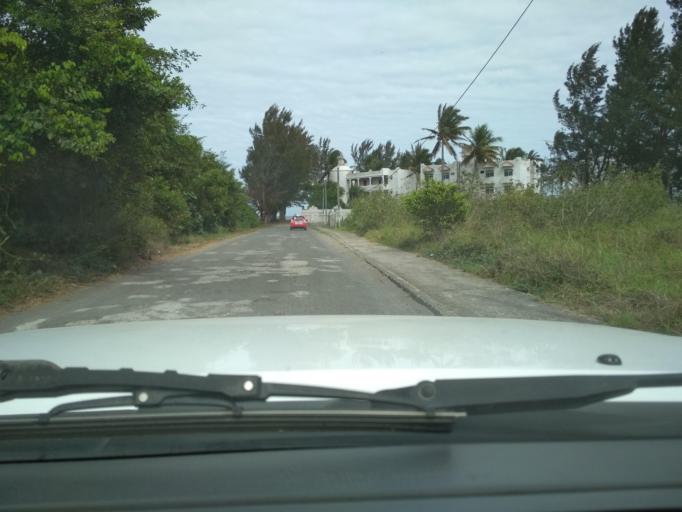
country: MX
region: Veracruz
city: Anton Lizardo
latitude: 19.0397
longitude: -95.9709
